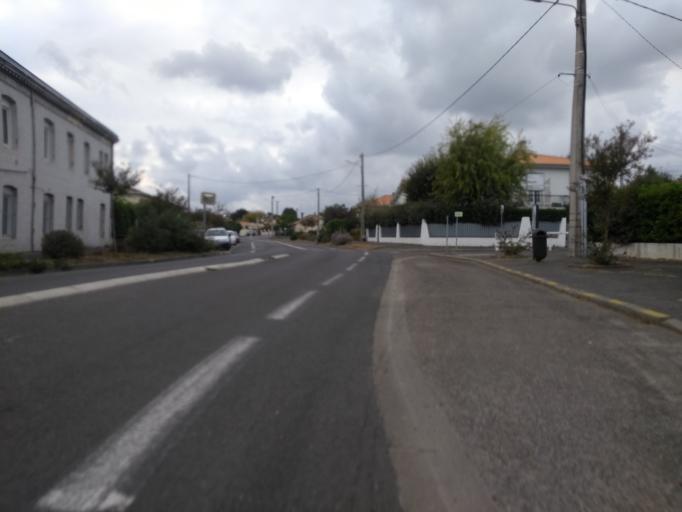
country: FR
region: Aquitaine
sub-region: Departement de la Gironde
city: Merignac
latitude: 44.8267
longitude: -0.6522
